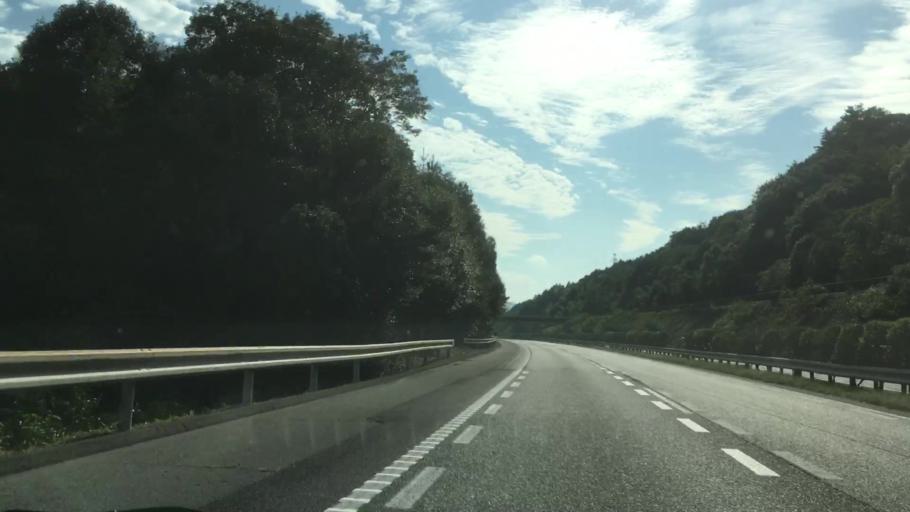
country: JP
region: Yamaguchi
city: Hikari
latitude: 34.0567
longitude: 132.0057
